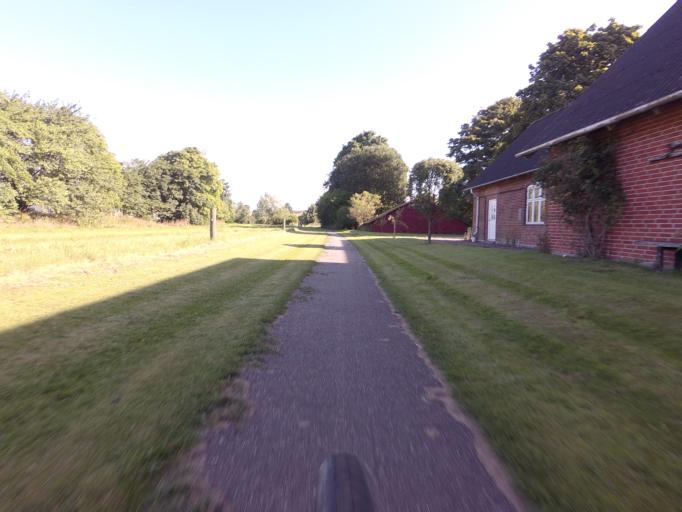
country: DK
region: Central Jutland
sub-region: Horsens Kommune
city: Horsens
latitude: 55.9450
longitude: 9.7849
